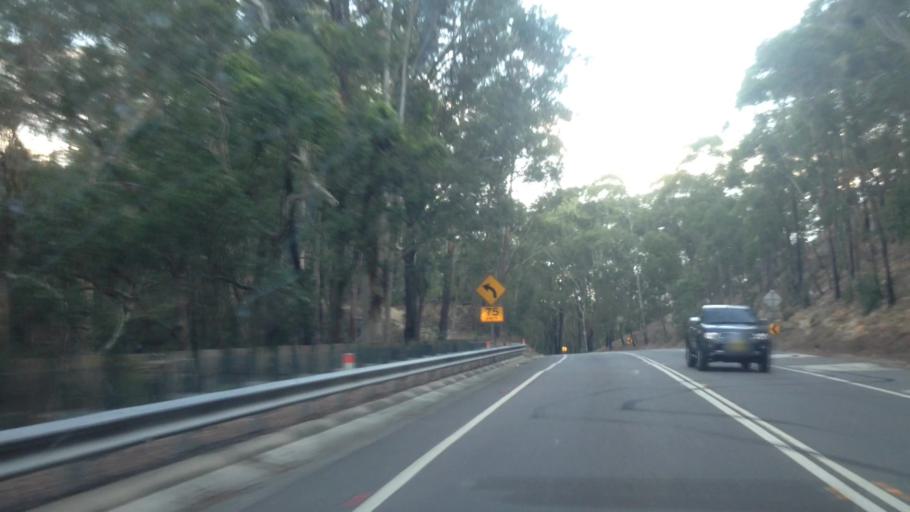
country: AU
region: New South Wales
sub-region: Lake Macquarie Shire
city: Cooranbong
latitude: -32.9675
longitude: 151.4799
